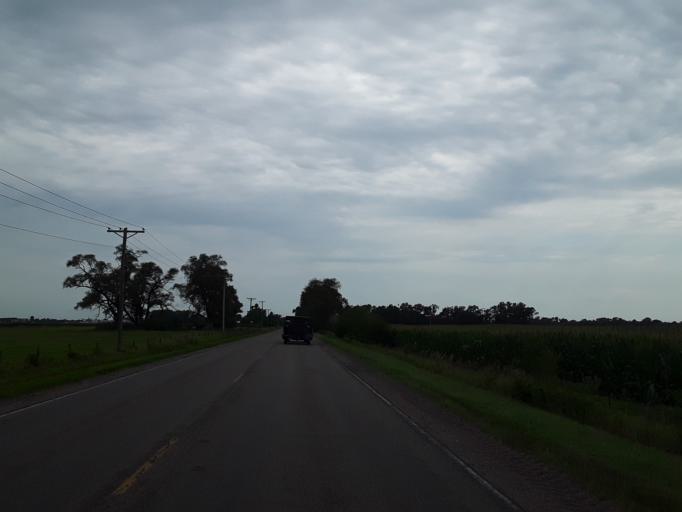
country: US
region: Nebraska
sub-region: Saunders County
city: Yutan
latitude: 41.2471
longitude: -96.3304
